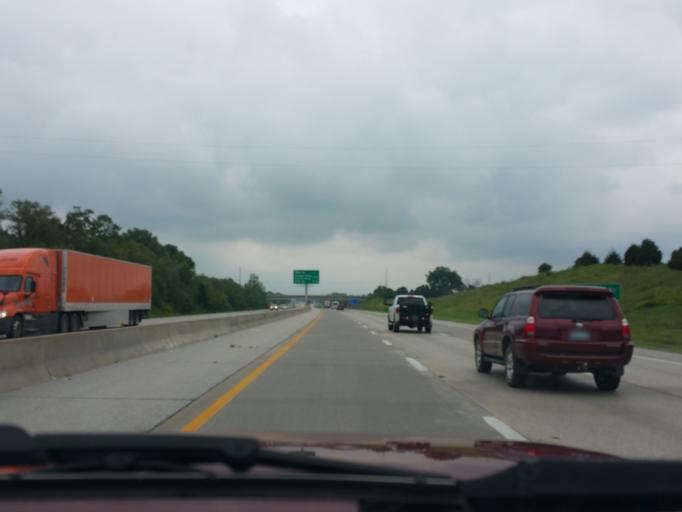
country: US
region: Kansas
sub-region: Wyandotte County
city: Edwardsville
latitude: 39.1047
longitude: -94.7843
